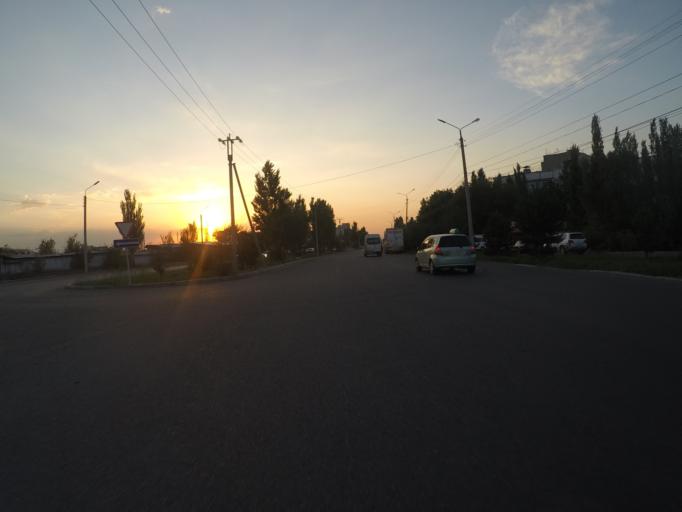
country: KG
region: Chuy
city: Bishkek
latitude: 42.8112
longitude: 74.6345
